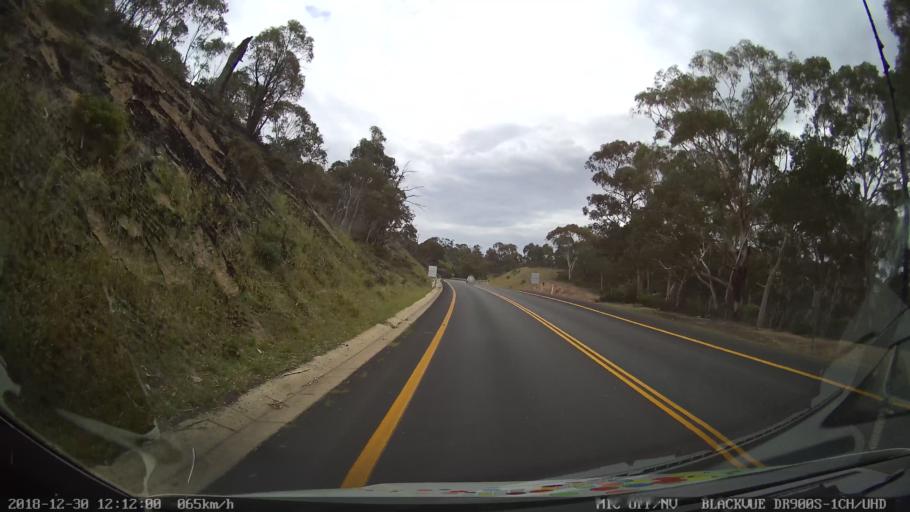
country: AU
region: New South Wales
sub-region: Snowy River
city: Jindabyne
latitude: -36.3612
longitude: 148.5874
